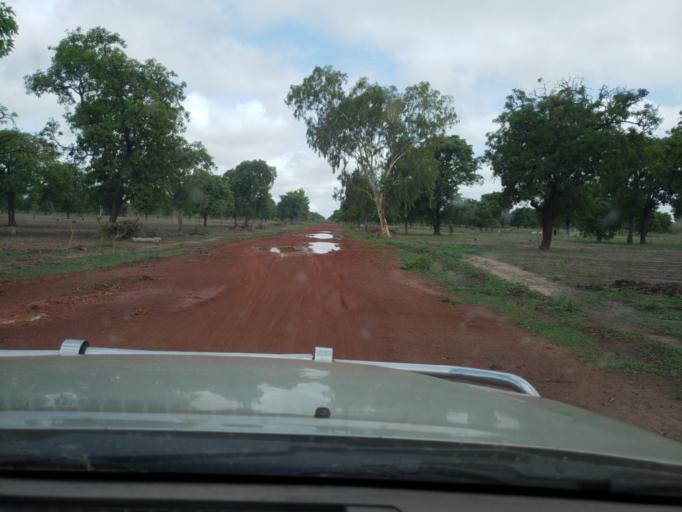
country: ML
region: Segou
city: Bla
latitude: 12.4597
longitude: -6.1591
